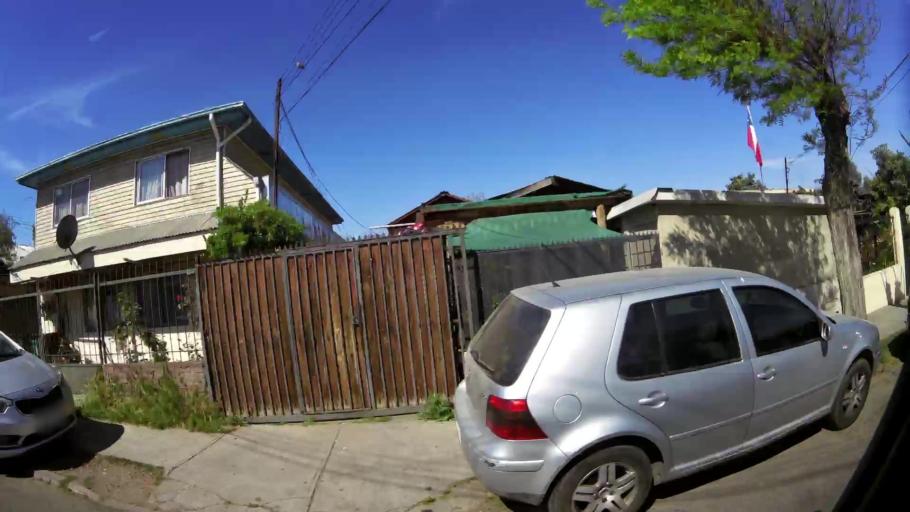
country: CL
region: Santiago Metropolitan
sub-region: Provincia de Santiago
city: Lo Prado
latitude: -33.4986
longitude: -70.7188
